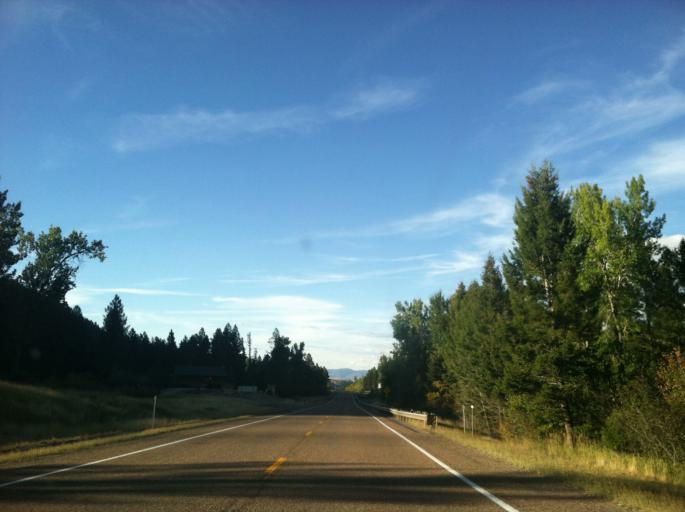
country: US
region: Montana
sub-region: Granite County
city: Philipsburg
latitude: 46.4646
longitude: -113.2349
